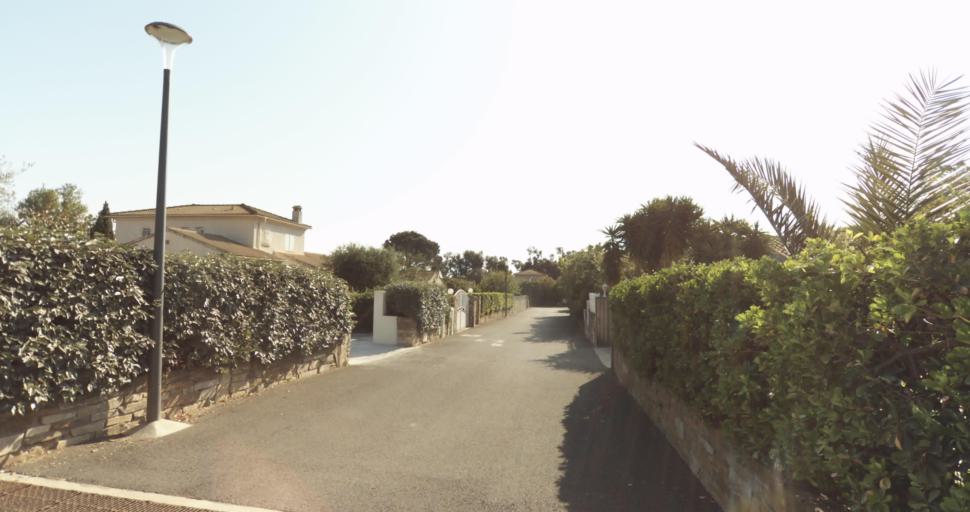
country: FR
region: Corsica
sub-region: Departement de la Haute-Corse
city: Biguglia
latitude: 42.6338
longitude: 9.4327
